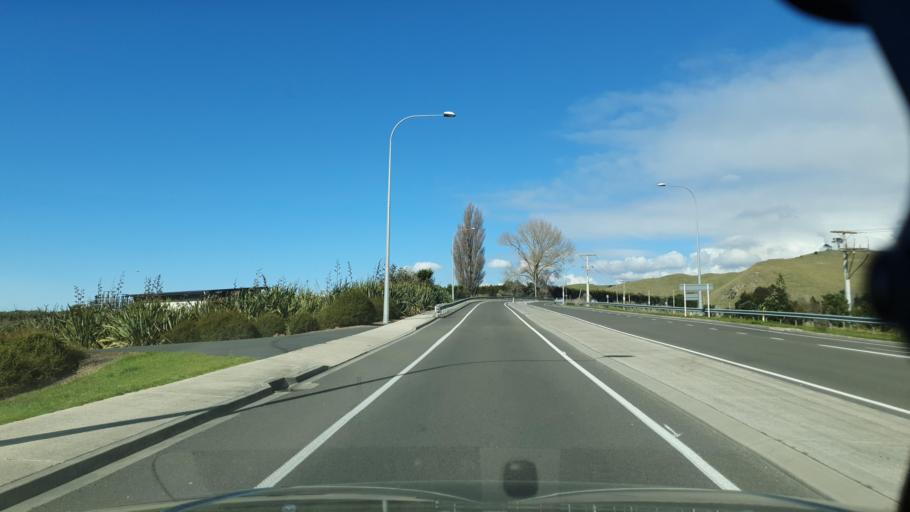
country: NZ
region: Bay of Plenty
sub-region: Tauranga City
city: Tauranga
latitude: -37.7155
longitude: 176.2833
